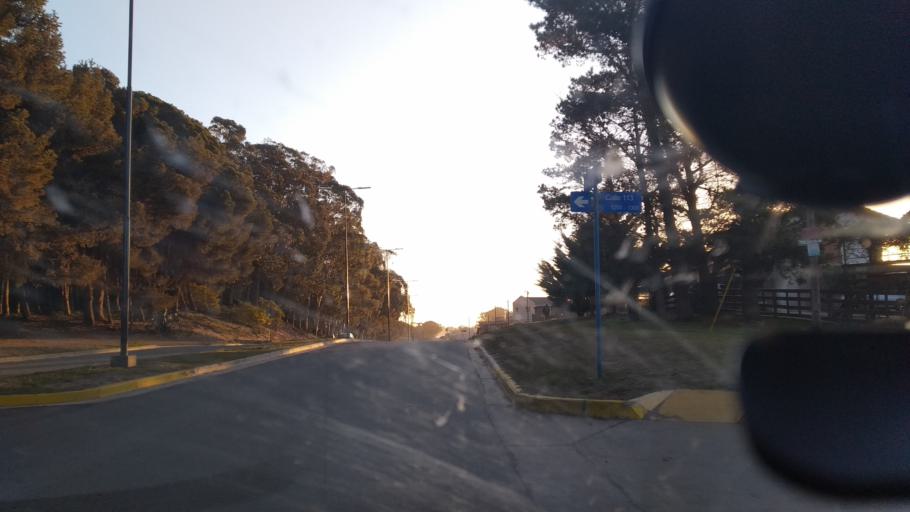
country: AR
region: Buenos Aires
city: Necochea
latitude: -38.5857
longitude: -58.7512
